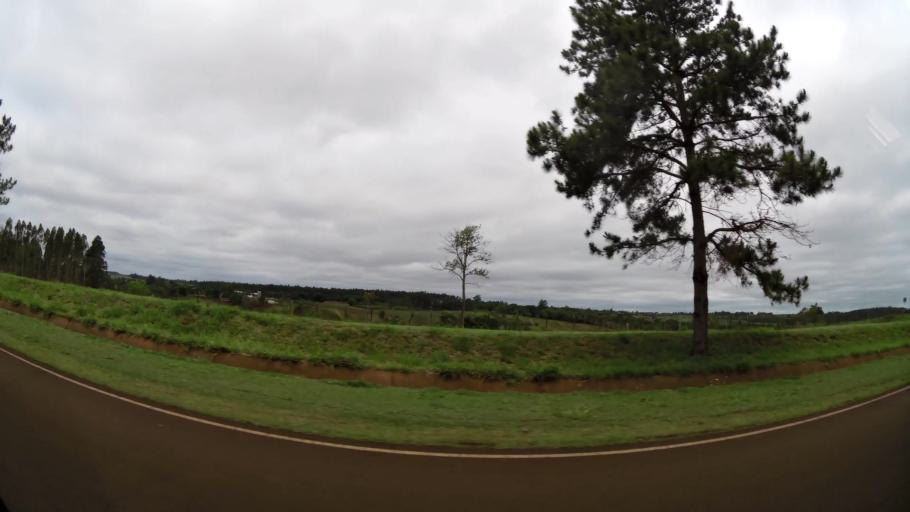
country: PY
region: Alto Parana
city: Colonia Yguazu
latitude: -25.4652
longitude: -54.8461
